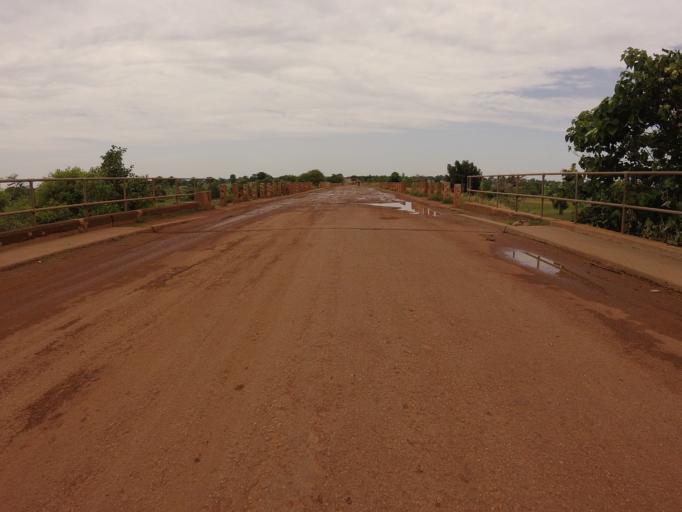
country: GH
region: Upper East
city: Bawku
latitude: 11.0025
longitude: -0.3836
